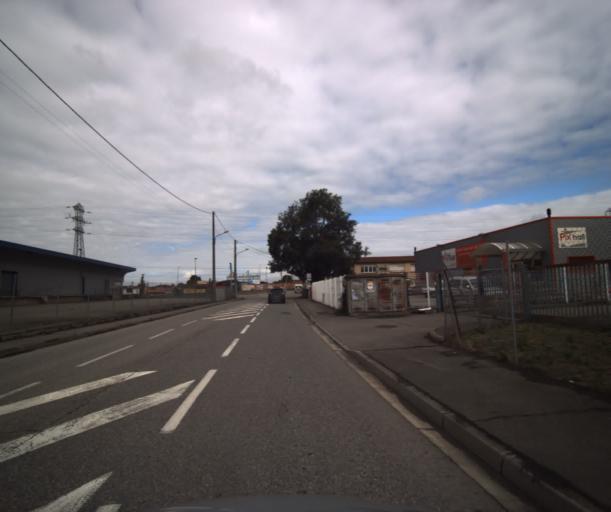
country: FR
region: Midi-Pyrenees
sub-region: Departement de la Haute-Garonne
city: Portet-sur-Garonne
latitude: 43.5512
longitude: 1.4105
